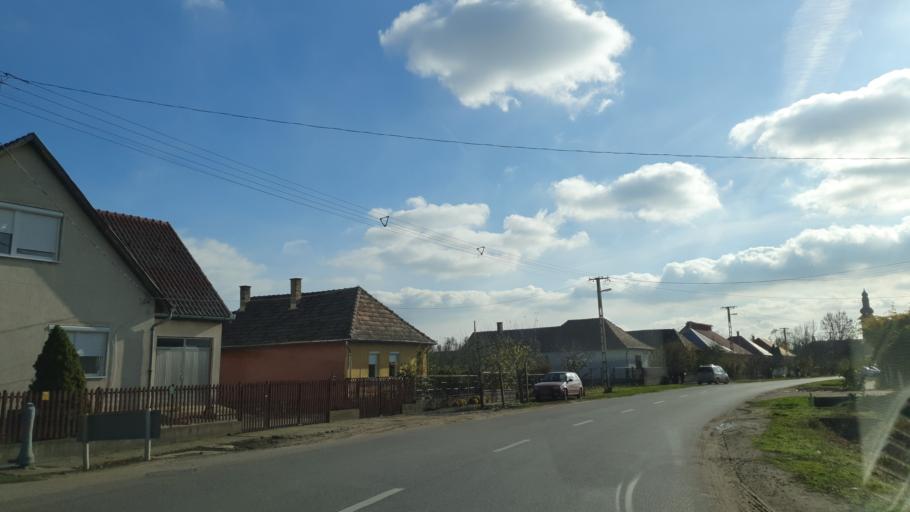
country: HU
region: Szabolcs-Szatmar-Bereg
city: Nyirkarasz
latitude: 48.1060
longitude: 22.0952
